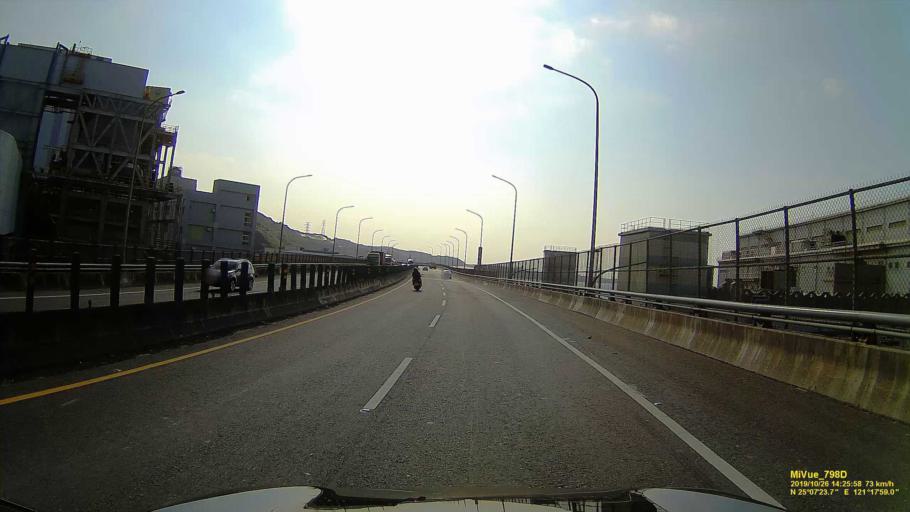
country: TW
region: Taiwan
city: Taoyuan City
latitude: 25.1236
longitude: 121.3015
